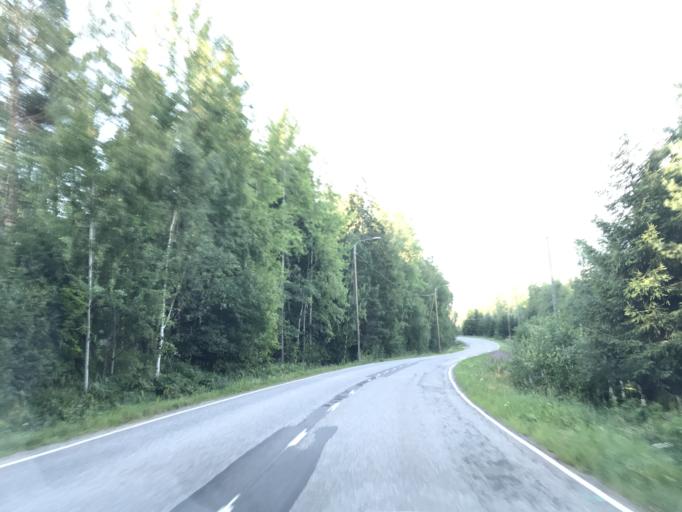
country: FI
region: Uusimaa
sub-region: Helsinki
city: Nurmijaervi
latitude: 60.3753
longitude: 24.6783
